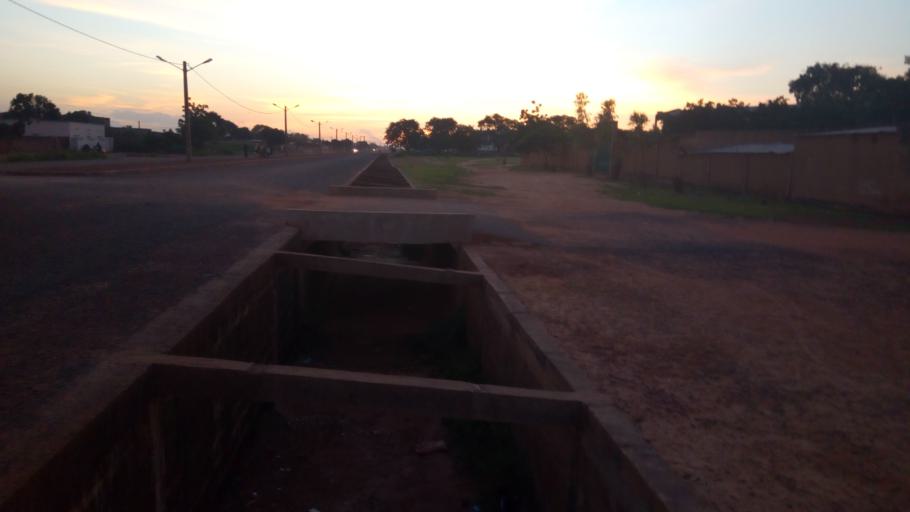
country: ML
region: Sikasso
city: Koutiala
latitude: 12.4011
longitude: -5.4476
